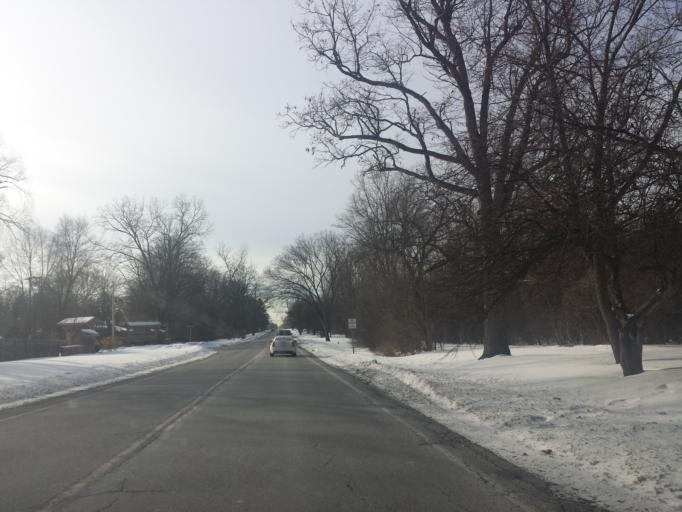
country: US
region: Michigan
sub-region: Oakland County
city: Franklin
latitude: 42.5392
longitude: -83.3409
